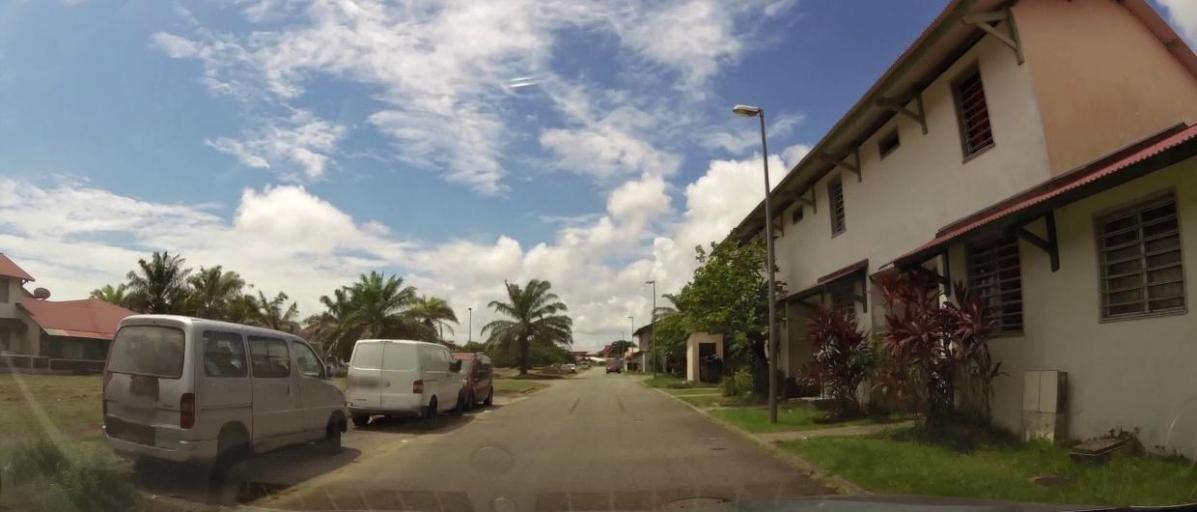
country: GF
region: Guyane
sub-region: Guyane
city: Kourou
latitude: 5.1691
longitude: -52.6553
